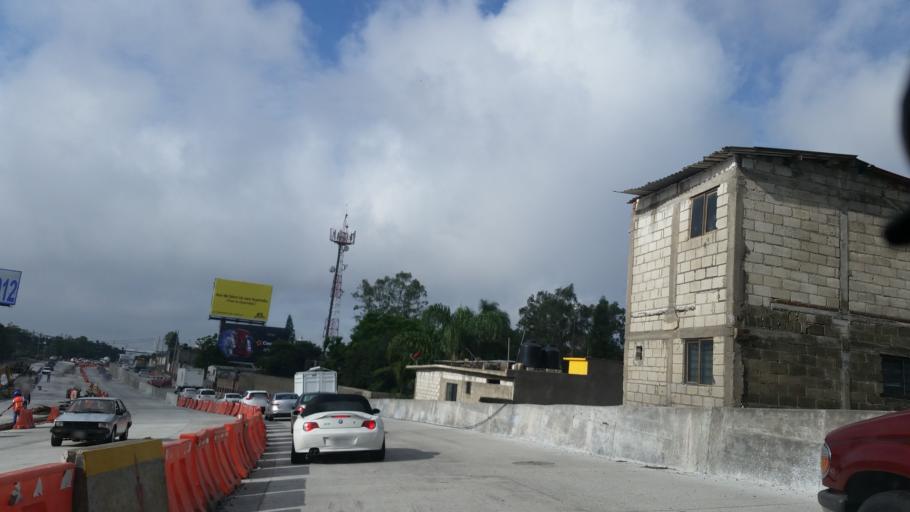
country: MX
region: Morelos
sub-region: Cuernavaca
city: Colonia los Cerritos
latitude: 18.9429
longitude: -99.1902
